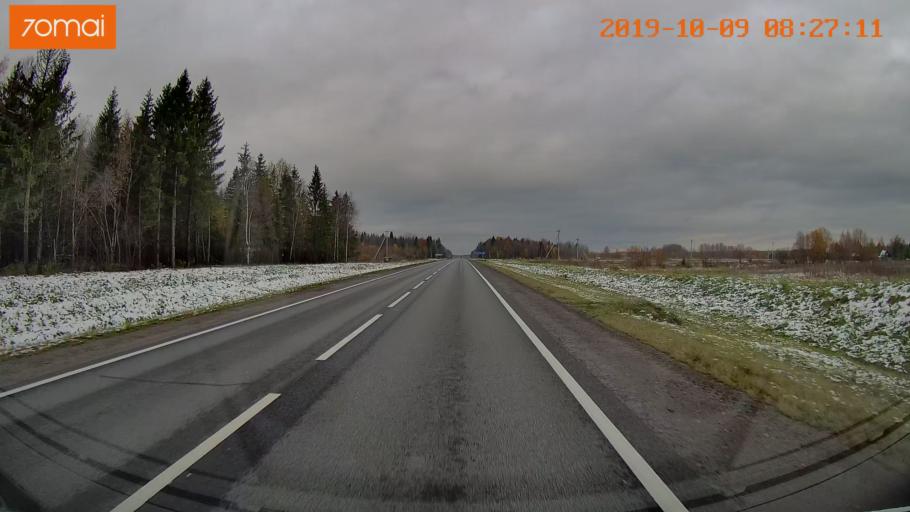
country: RU
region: Vologda
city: Gryazovets
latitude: 58.8005
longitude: 40.2529
